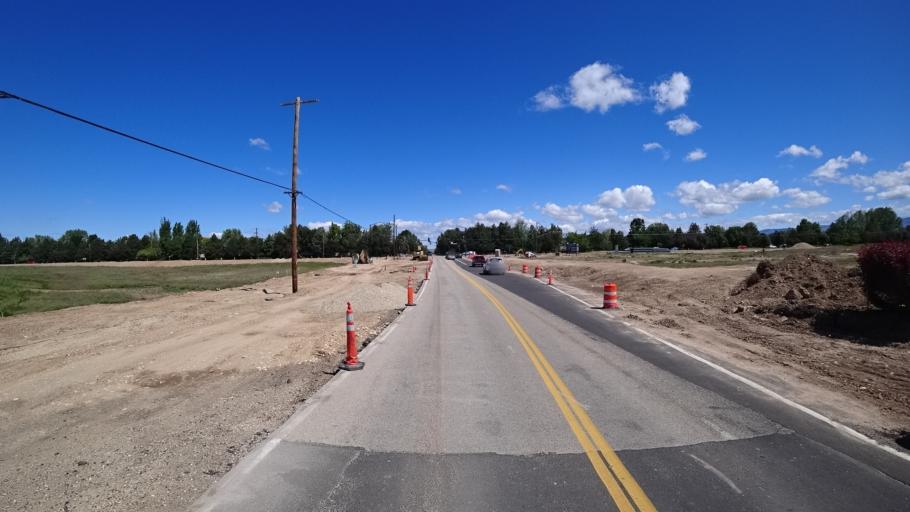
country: US
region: Idaho
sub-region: Ada County
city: Eagle
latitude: 43.6617
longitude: -116.3745
